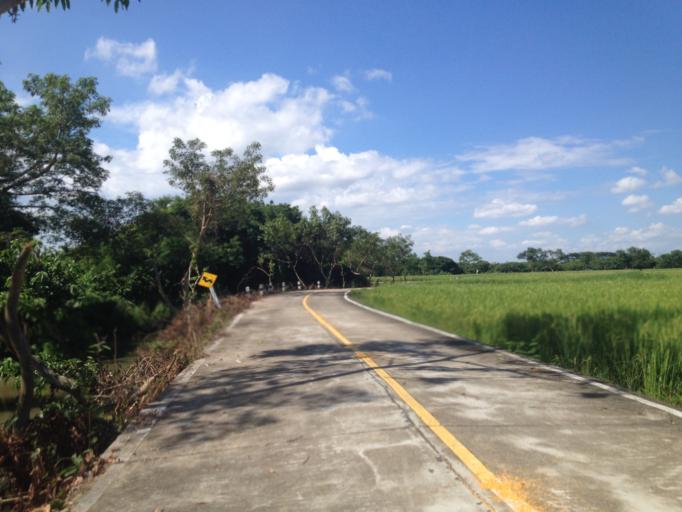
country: TH
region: Chiang Mai
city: Saraphi
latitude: 18.6905
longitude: 98.9803
